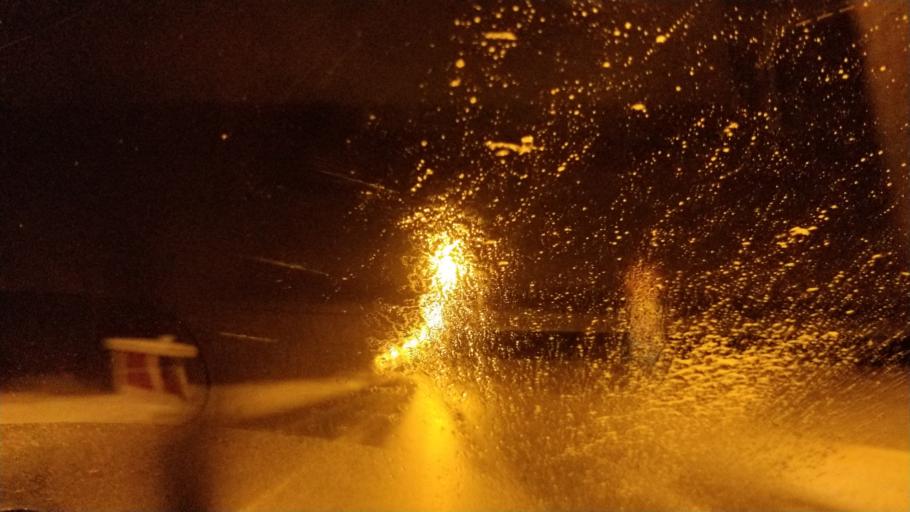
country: FI
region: Lapland
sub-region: Kemi-Tornio
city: Tervola
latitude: 66.1422
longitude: 24.9511
